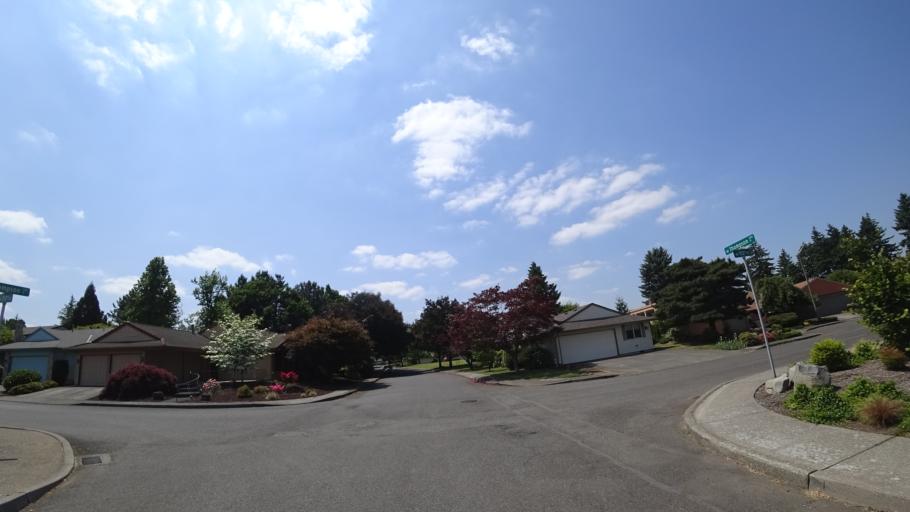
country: US
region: Oregon
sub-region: Multnomah County
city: Fairview
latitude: 45.5400
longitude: -122.5056
